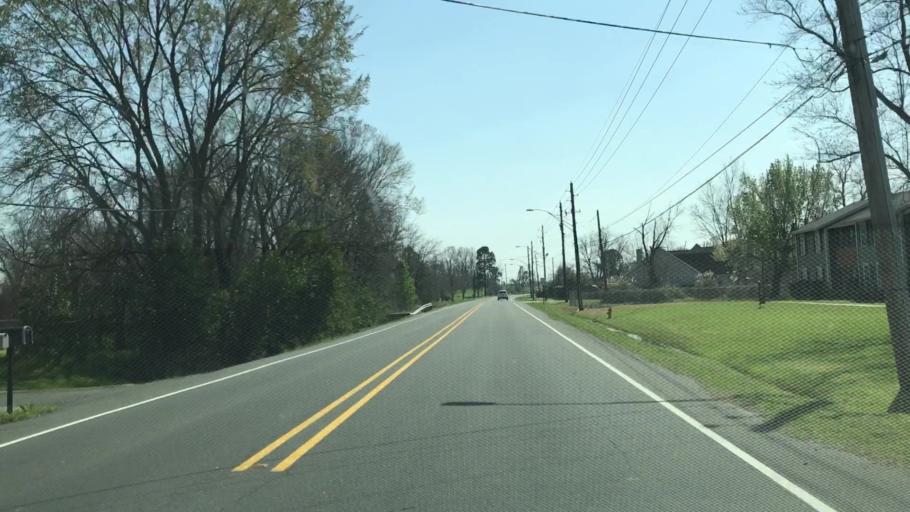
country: US
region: Louisiana
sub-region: Bossier Parish
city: Bossier City
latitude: 32.4108
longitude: -93.6914
